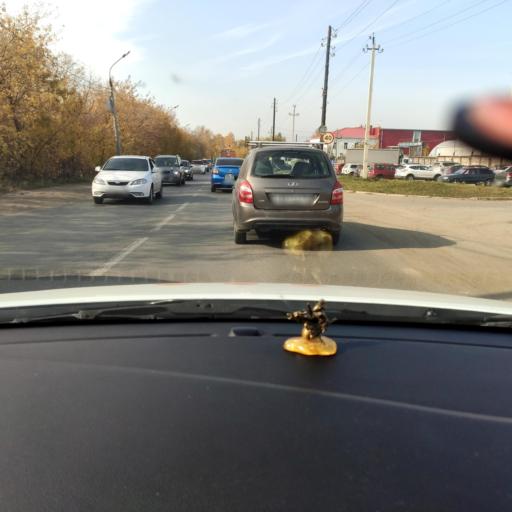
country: RU
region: Tatarstan
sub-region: Gorod Kazan'
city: Kazan
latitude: 55.7776
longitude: 49.1956
